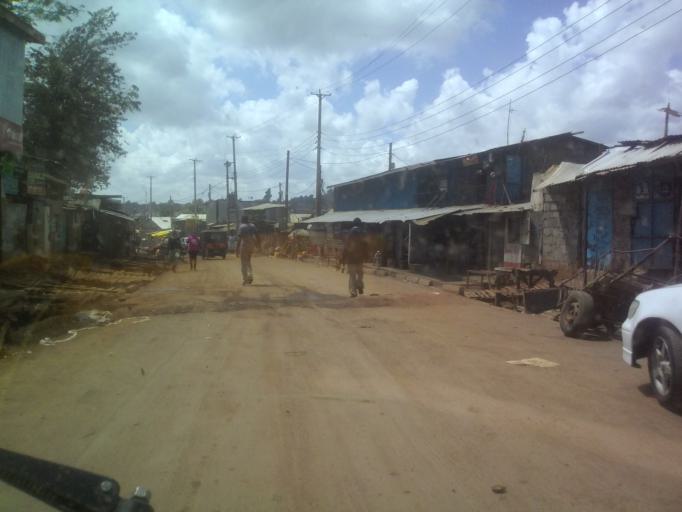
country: KE
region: Nairobi Area
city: Nairobi
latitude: -1.3113
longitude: 36.7747
